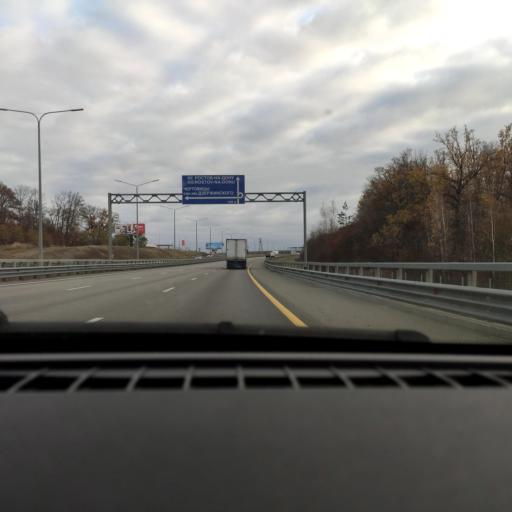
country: RU
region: Voronezj
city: Ramon'
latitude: 51.8283
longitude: 39.2456
